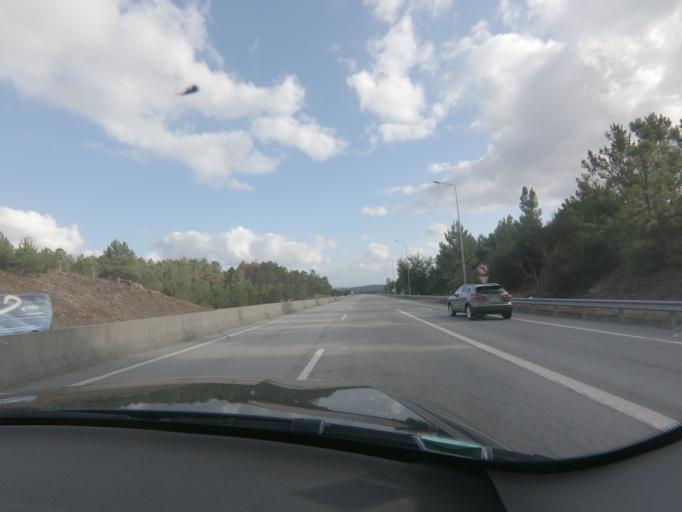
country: PT
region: Viseu
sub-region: Viseu
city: Abraveses
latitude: 40.6745
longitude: -7.9684
